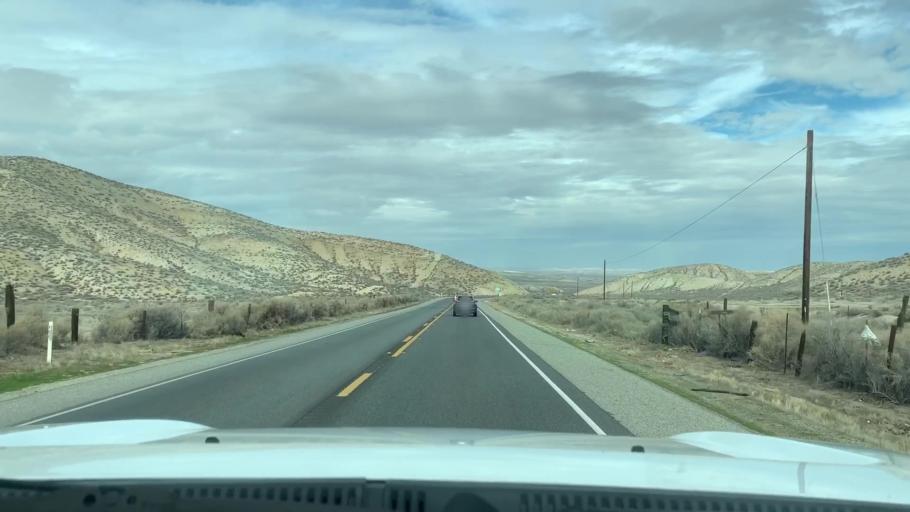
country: US
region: California
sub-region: Kern County
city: Maricopa
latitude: 35.0288
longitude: -119.4186
